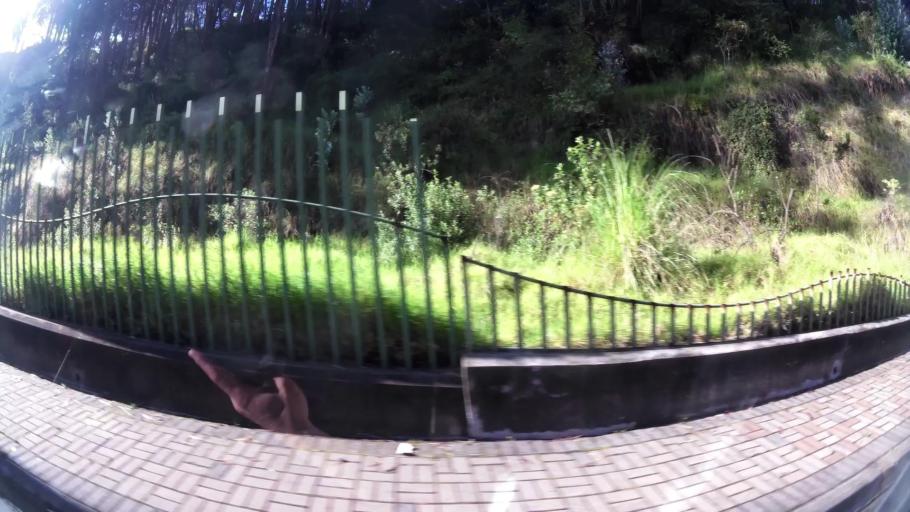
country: EC
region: Pichincha
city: Quito
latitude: -0.2346
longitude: -78.5162
